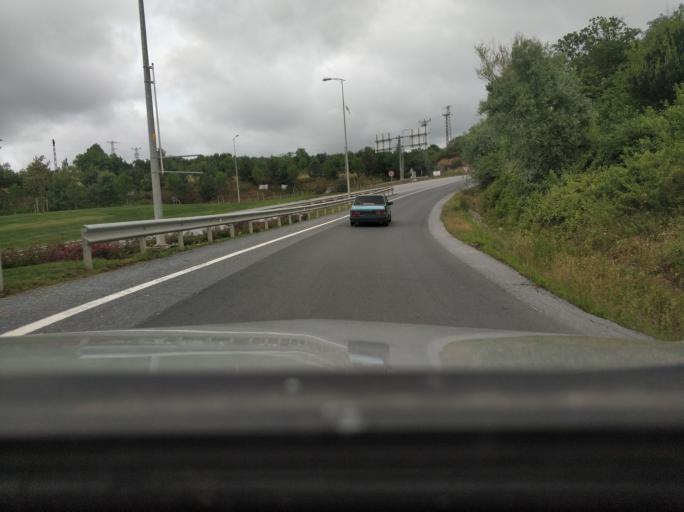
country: TR
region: Istanbul
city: Kemerburgaz
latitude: 41.1621
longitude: 28.8946
